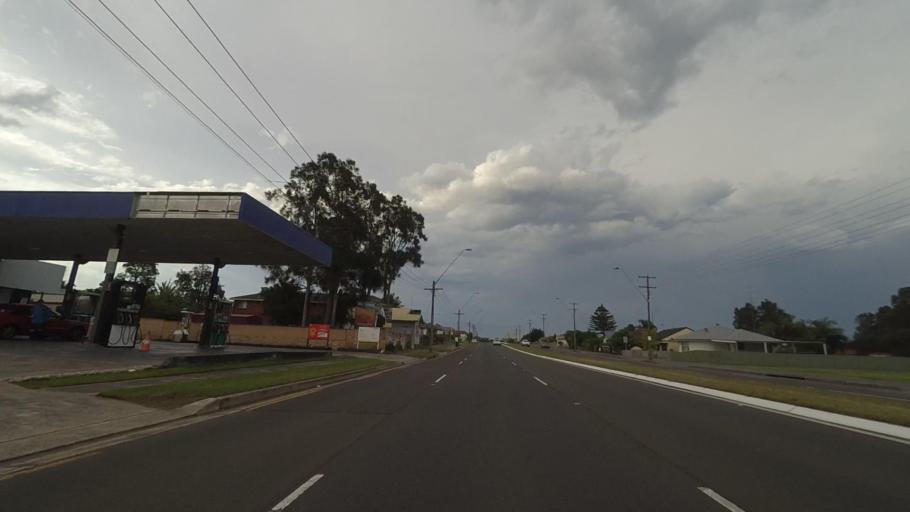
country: AU
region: New South Wales
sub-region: Shellharbour
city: Barrack Heights
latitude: -34.5573
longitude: 150.8595
